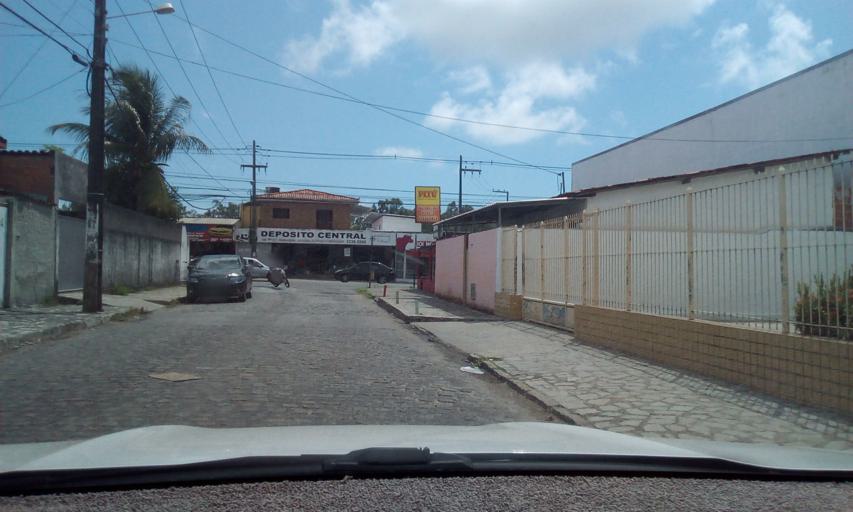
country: BR
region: Paraiba
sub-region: Joao Pessoa
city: Joao Pessoa
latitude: -7.1878
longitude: -34.8397
